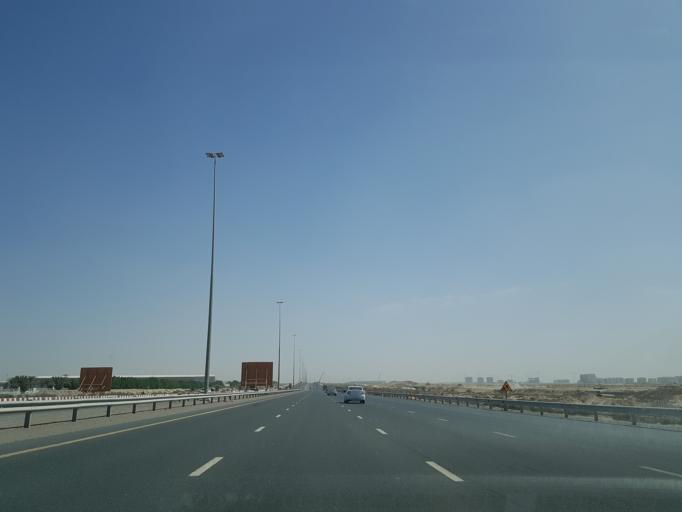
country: AE
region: Dubai
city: Dubai
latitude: 24.9624
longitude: 55.1912
